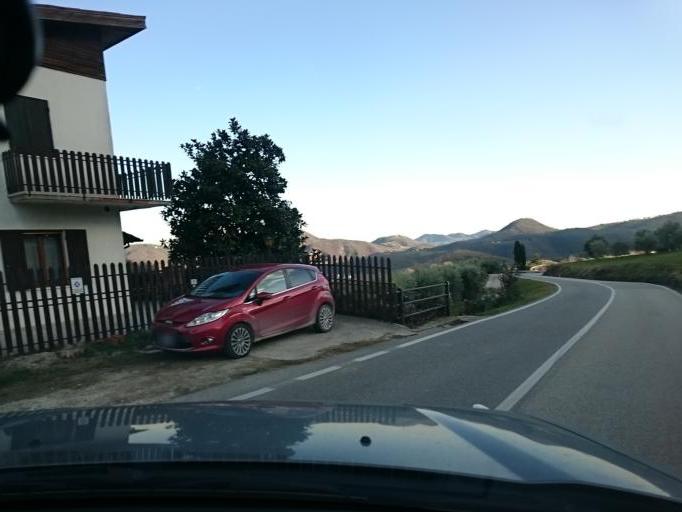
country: IT
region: Veneto
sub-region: Provincia di Padova
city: Treponti
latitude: 45.3682
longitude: 11.6807
